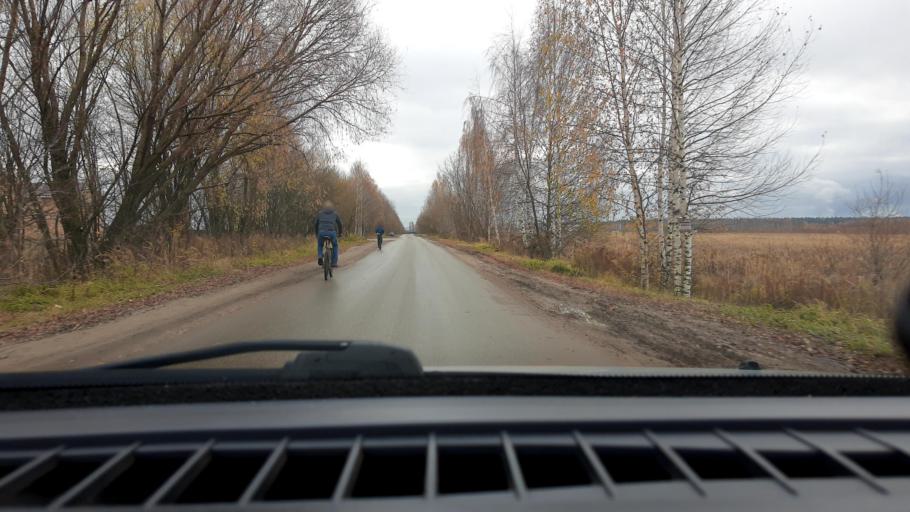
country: RU
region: Nizjnij Novgorod
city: Afonino
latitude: 56.1999
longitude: 44.1331
